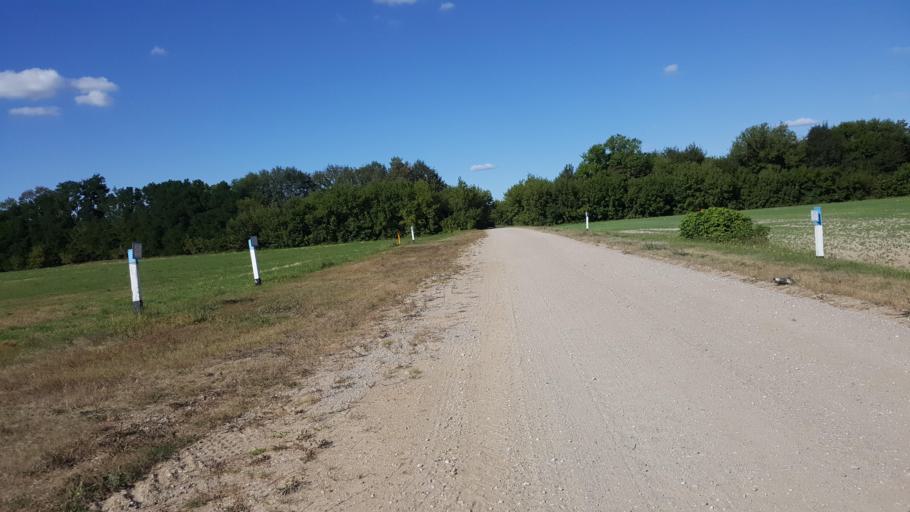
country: BY
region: Brest
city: Vysokaye
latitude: 52.3243
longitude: 23.5497
